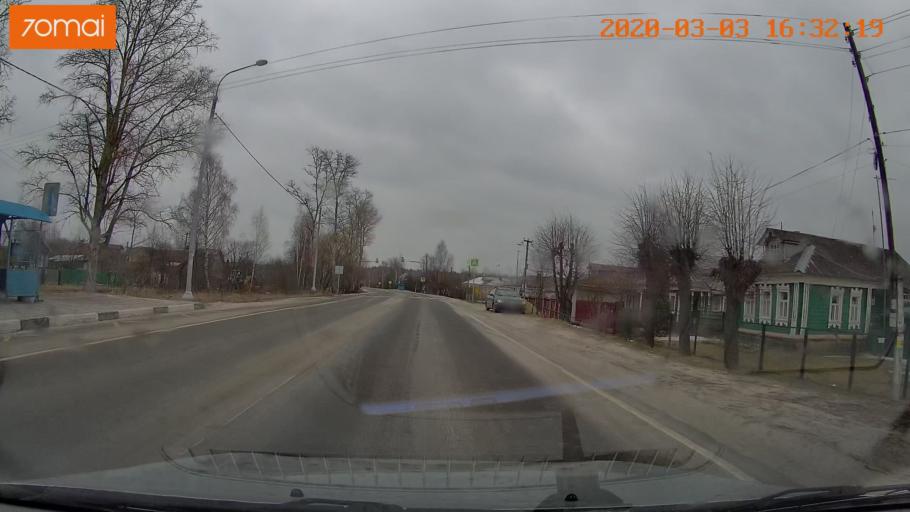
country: RU
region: Moskovskaya
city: Konobeyevo
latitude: 55.4209
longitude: 38.7323
